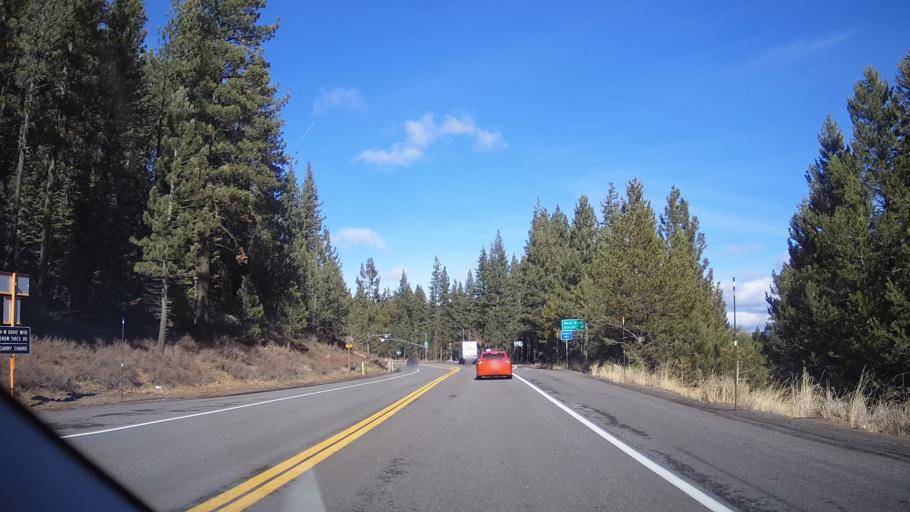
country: US
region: California
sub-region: Nevada County
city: Truckee
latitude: 39.3128
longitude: -120.2043
